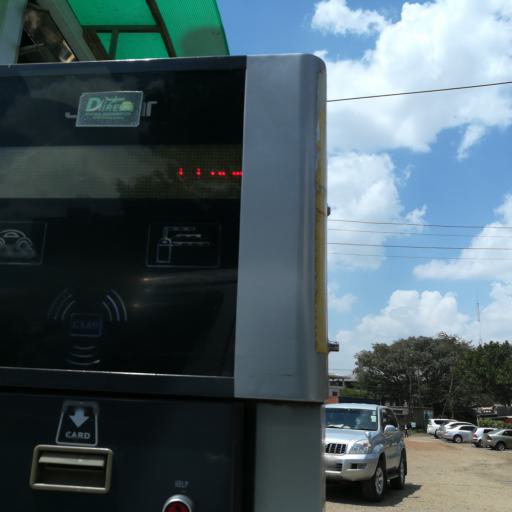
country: KE
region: Nairobi Area
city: Nairobi
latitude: -1.3165
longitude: 36.8144
